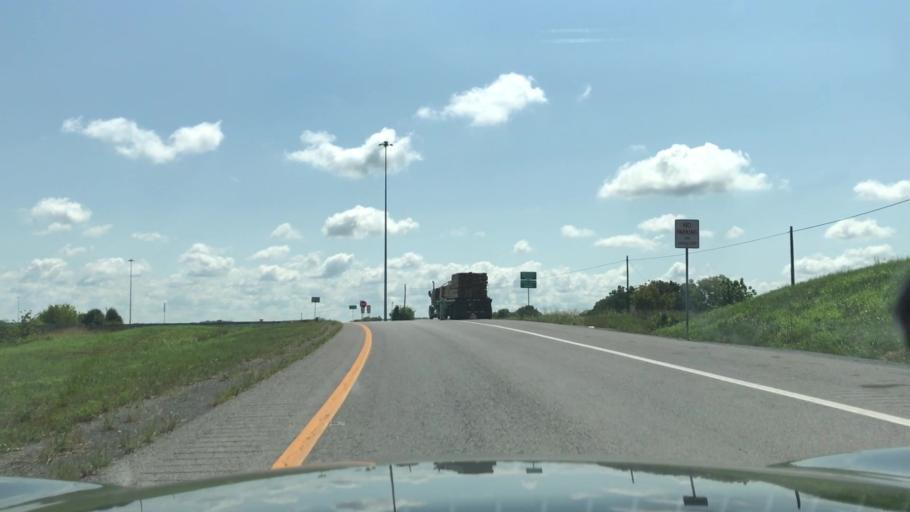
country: US
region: Kentucky
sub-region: Adair County
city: Columbia
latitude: 37.0725
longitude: -85.3409
